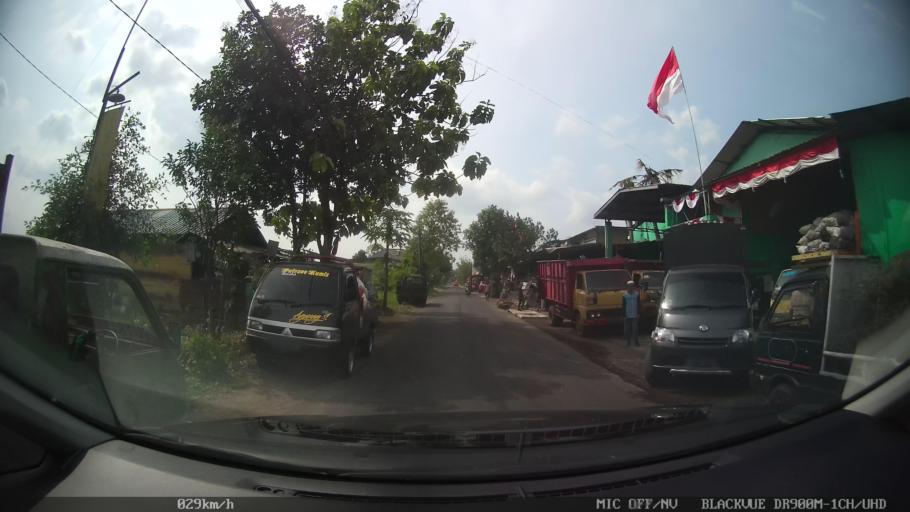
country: ID
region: Daerah Istimewa Yogyakarta
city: Depok
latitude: -7.7990
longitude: 110.4453
